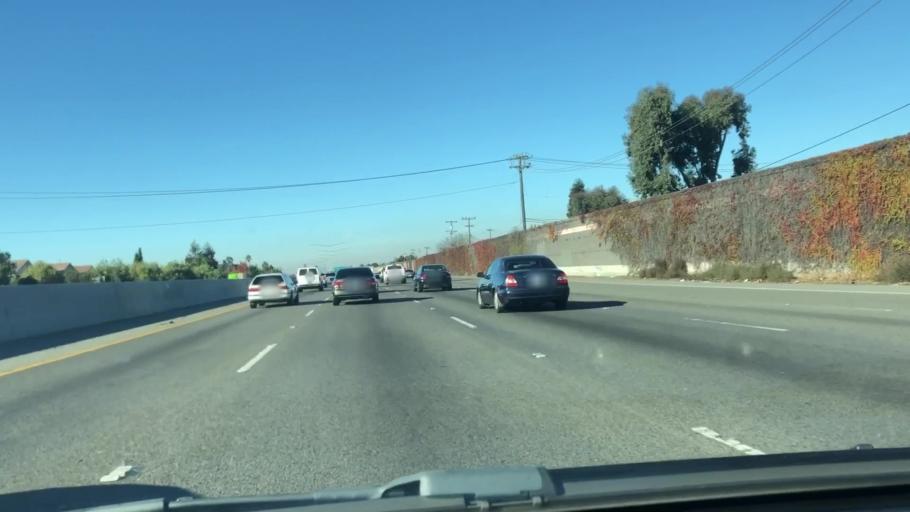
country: US
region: California
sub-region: Alameda County
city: Newark
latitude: 37.5509
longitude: -122.0254
